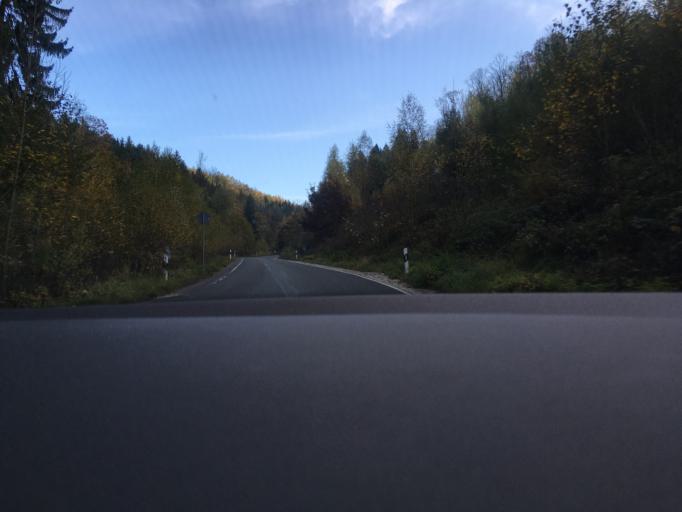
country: DE
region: Saxony
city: Glashutte
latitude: 50.8515
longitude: 13.7948
